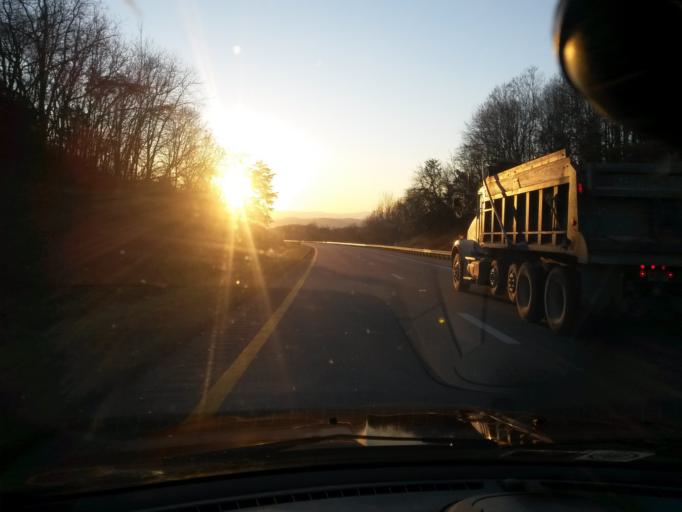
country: US
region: Virginia
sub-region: City of Lexington
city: Lexington
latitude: 37.8882
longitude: -79.5611
